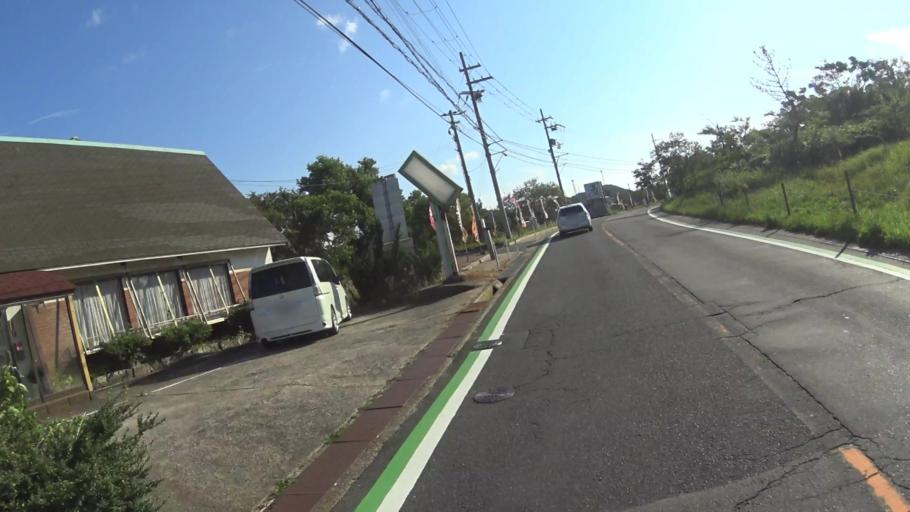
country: JP
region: Hyogo
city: Toyooka
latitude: 35.6594
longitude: 134.9635
